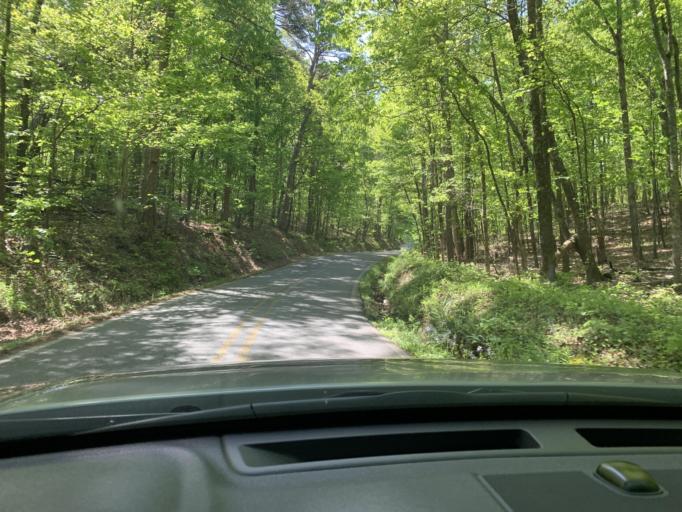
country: US
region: Georgia
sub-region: Haralson County
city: Buchanan
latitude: 33.9117
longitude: -85.2011
